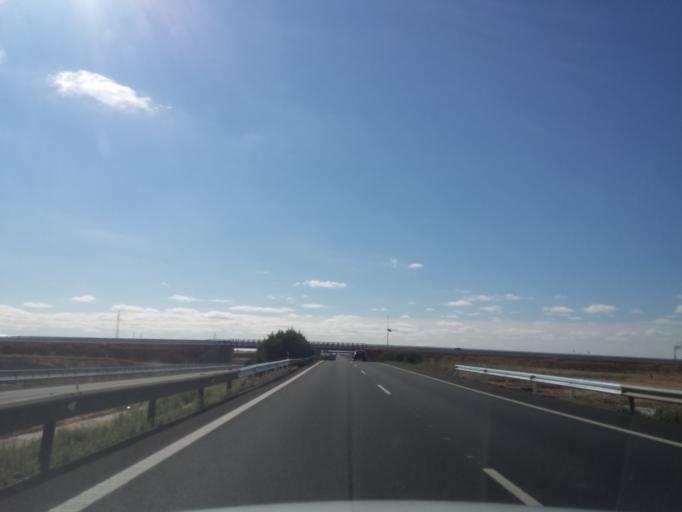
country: ES
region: Castille and Leon
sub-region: Provincia de Zamora
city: Castrogonzalo
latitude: 41.9684
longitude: -5.5956
